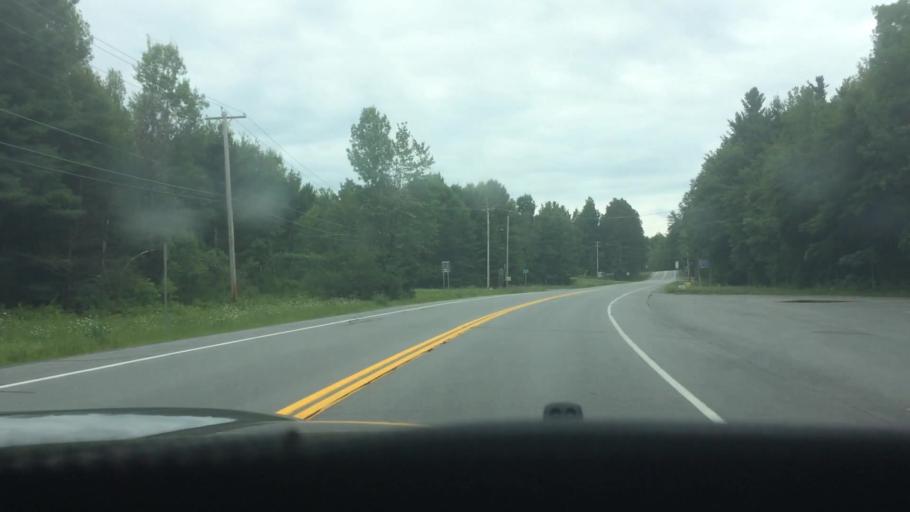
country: US
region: New York
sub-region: St. Lawrence County
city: Hannawa Falls
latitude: 44.5473
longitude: -74.9321
